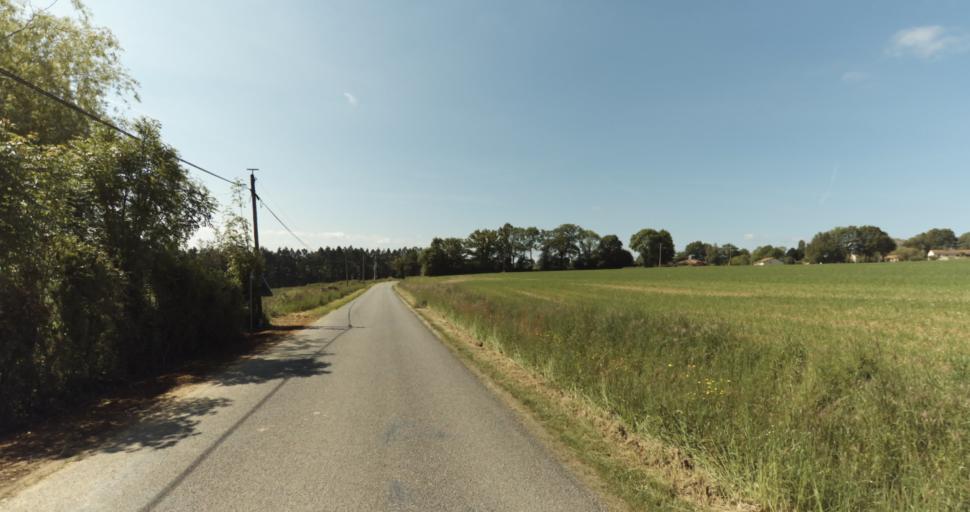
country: FR
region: Limousin
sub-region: Departement de la Haute-Vienne
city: Le Vigen
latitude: 45.7342
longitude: 1.2885
